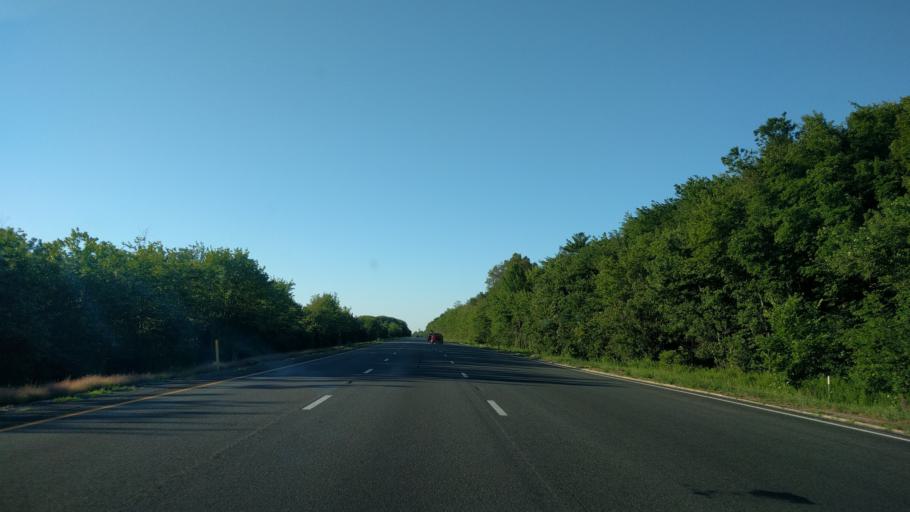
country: US
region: Massachusetts
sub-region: Worcester County
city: Milford
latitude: 42.1433
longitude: -71.4832
